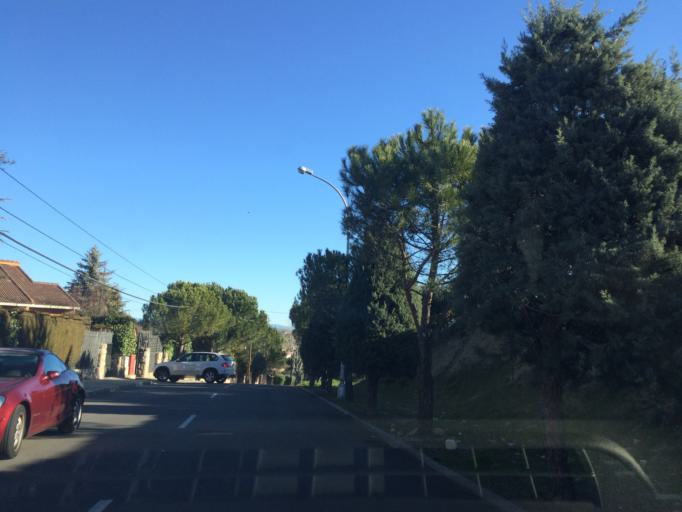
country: ES
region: Madrid
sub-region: Provincia de Madrid
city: Tres Cantos
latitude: 40.6098
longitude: -3.6857
